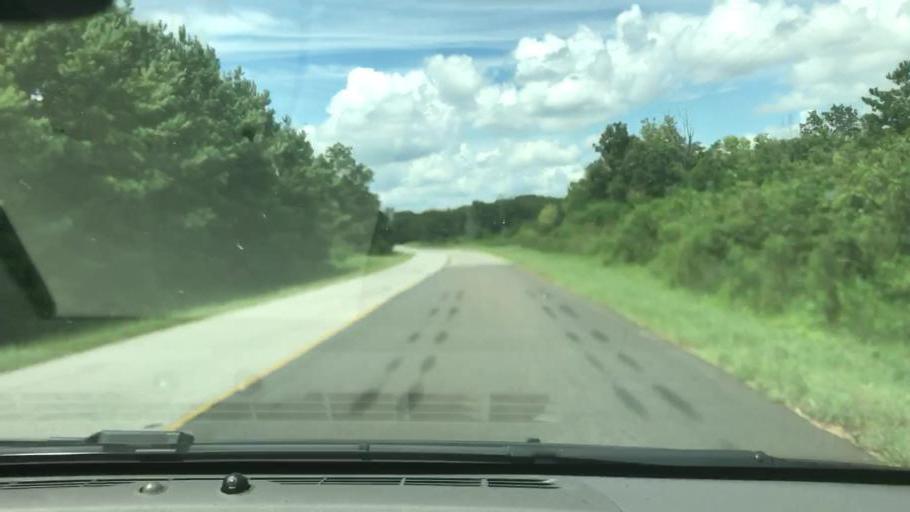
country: US
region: Georgia
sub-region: Stewart County
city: Lumpkin
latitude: 32.1335
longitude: -84.9924
